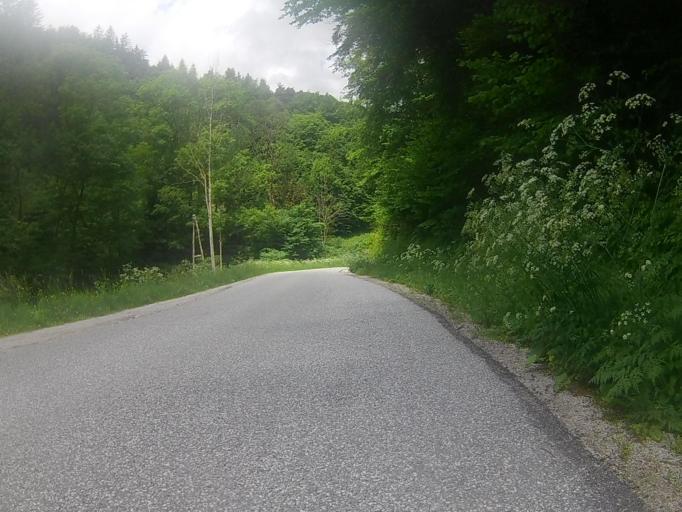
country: SI
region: Maribor
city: Bresternica
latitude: 46.5946
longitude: 15.5550
